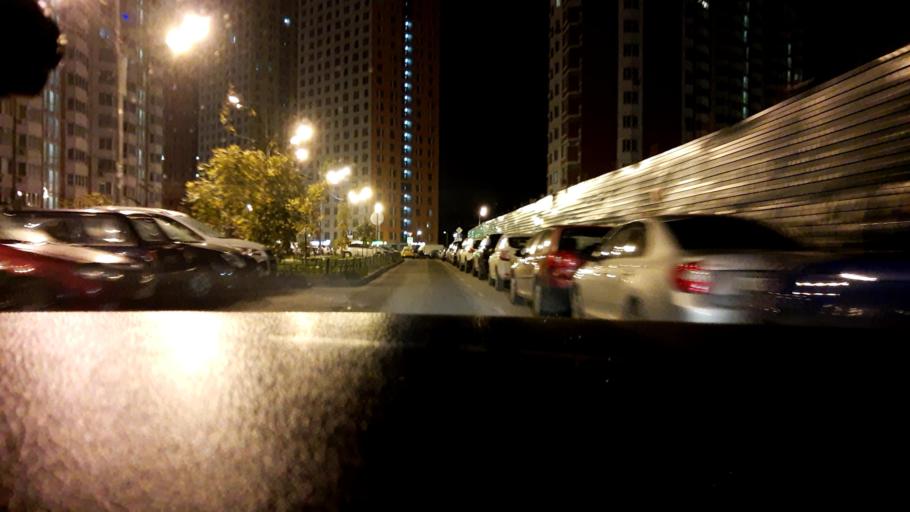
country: RU
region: Moscow
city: Khimki
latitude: 55.8740
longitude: 37.3936
